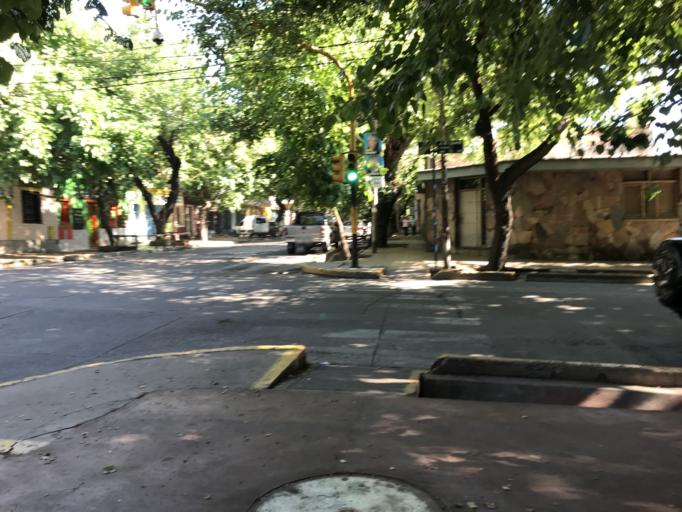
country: AR
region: Mendoza
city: Mendoza
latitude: -32.8802
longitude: -68.8308
